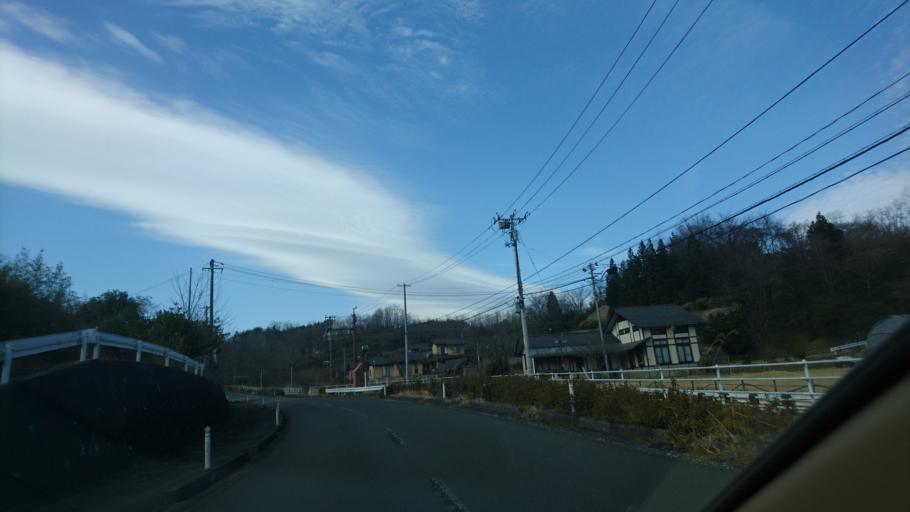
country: JP
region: Miyagi
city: Furukawa
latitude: 38.8047
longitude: 140.9047
